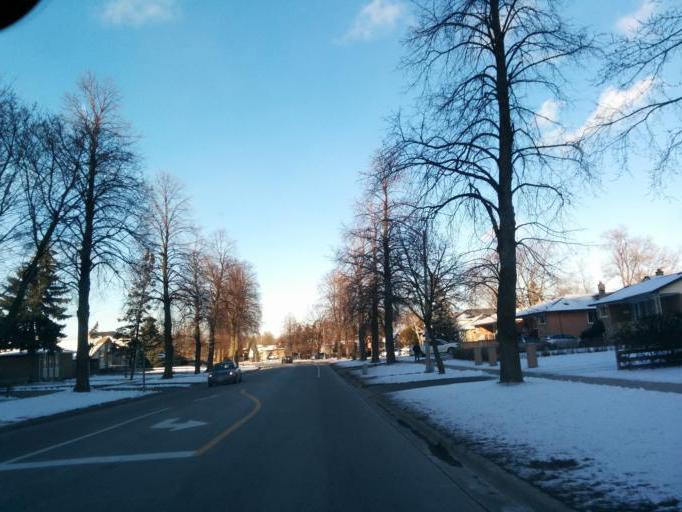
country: CA
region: Ontario
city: Mississauga
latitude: 43.5152
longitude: -79.6440
